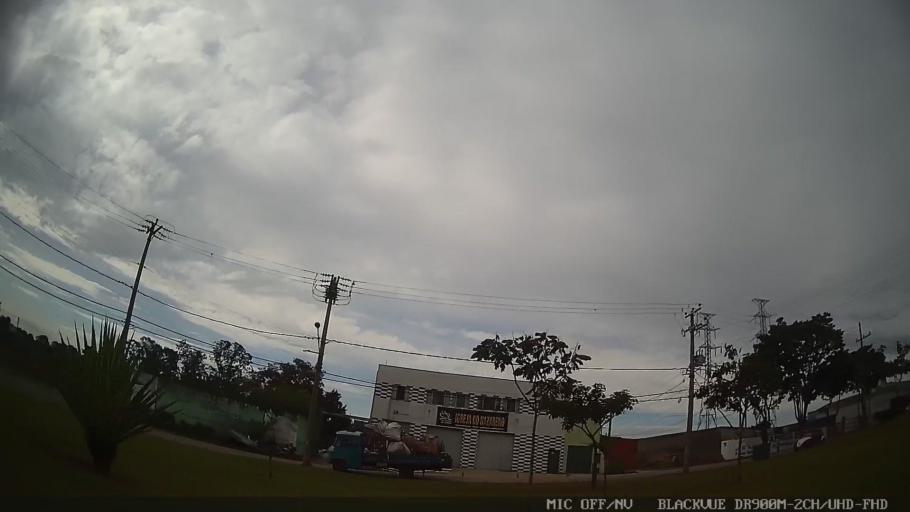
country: BR
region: Sao Paulo
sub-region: Salto
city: Salto
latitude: -23.2134
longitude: -47.2859
